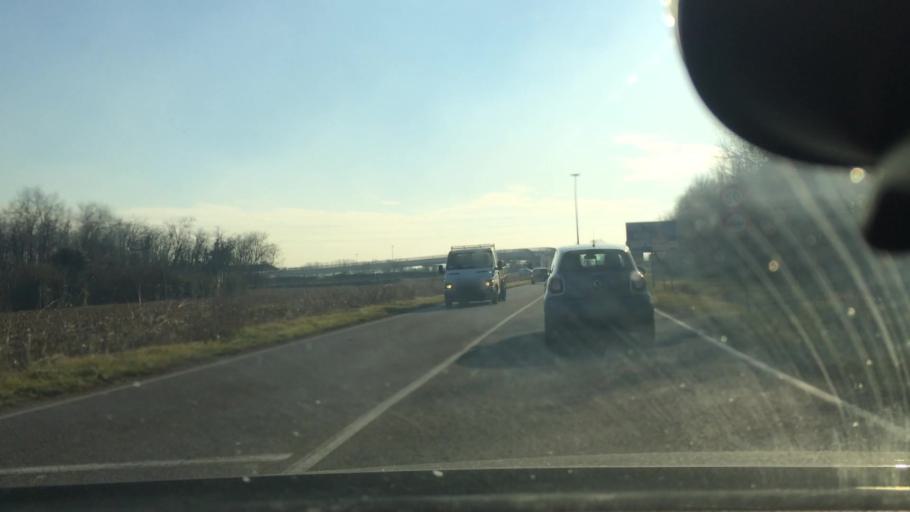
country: IT
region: Lombardy
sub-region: Citta metropolitana di Milano
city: Arluno
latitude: 45.5040
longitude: 8.9298
